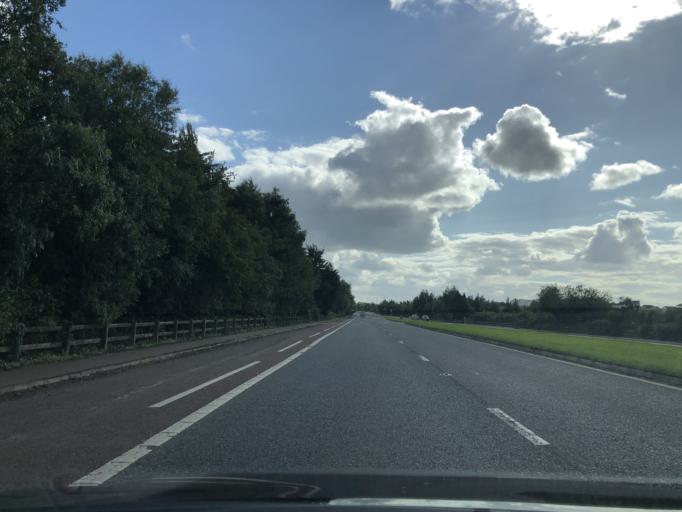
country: GB
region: Northern Ireland
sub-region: Ards District
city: Comber
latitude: 54.5571
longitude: -5.7174
